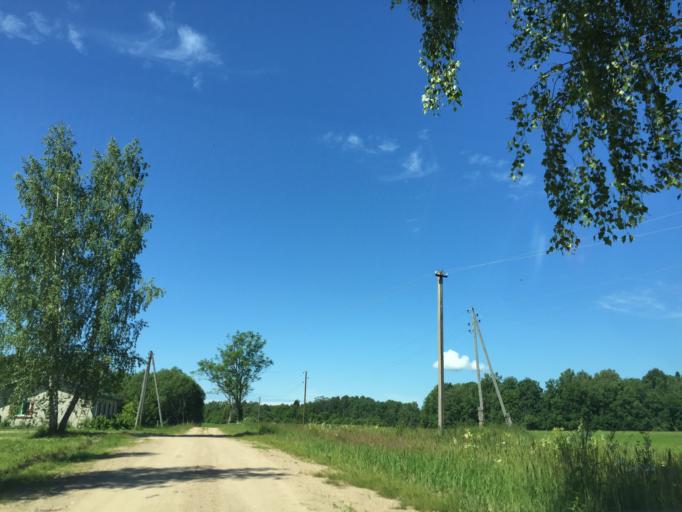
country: LV
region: Sigulda
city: Sigulda
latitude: 57.2223
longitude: 24.9337
